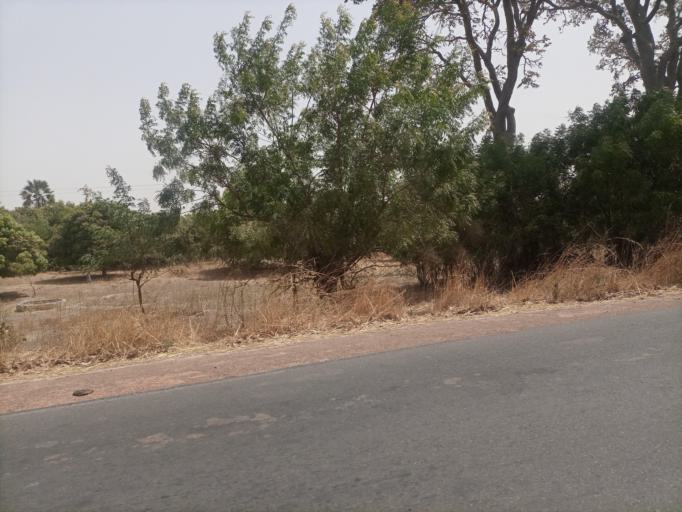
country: SN
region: Fatick
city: Sokone
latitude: 13.7338
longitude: -16.4225
